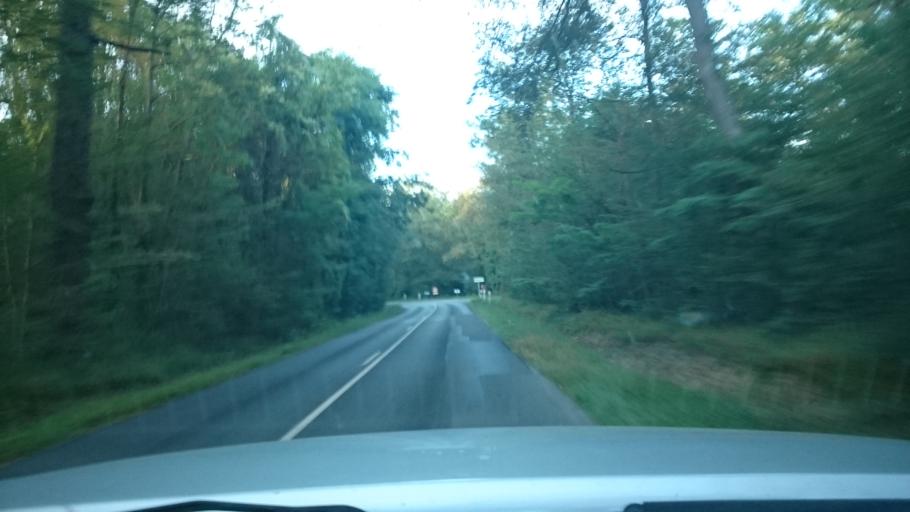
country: FR
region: Ile-de-France
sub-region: Departement de Seine-et-Marne
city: Samois-sur-Seine
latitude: 48.4666
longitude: 2.7373
